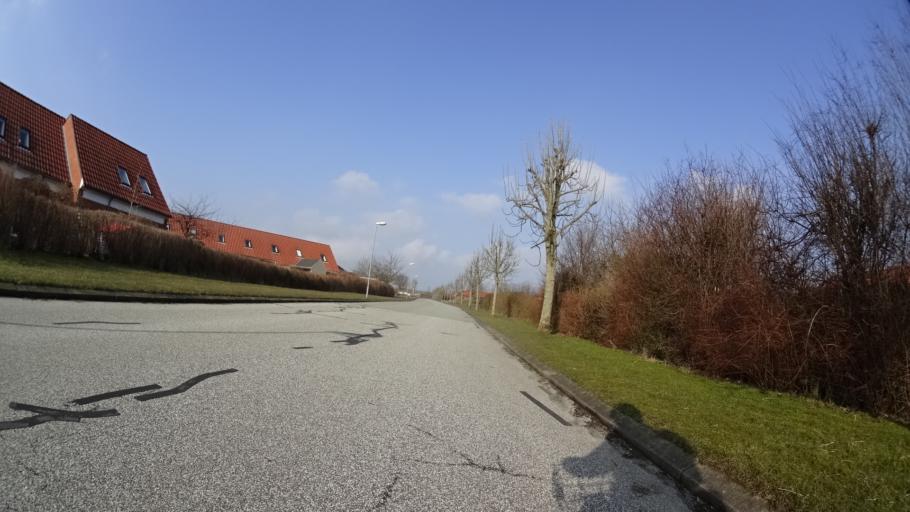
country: DK
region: Central Jutland
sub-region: Arhus Kommune
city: Tranbjerg
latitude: 56.0854
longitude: 10.1357
